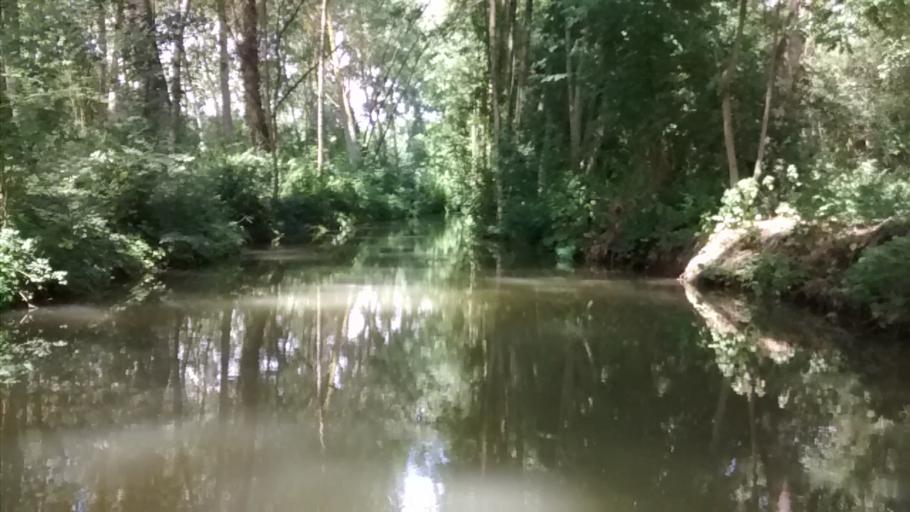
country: FR
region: Poitou-Charentes
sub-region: Departement des Deux-Sevres
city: Saint-Hilaire-la-Palud
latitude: 46.3017
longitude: -0.6918
